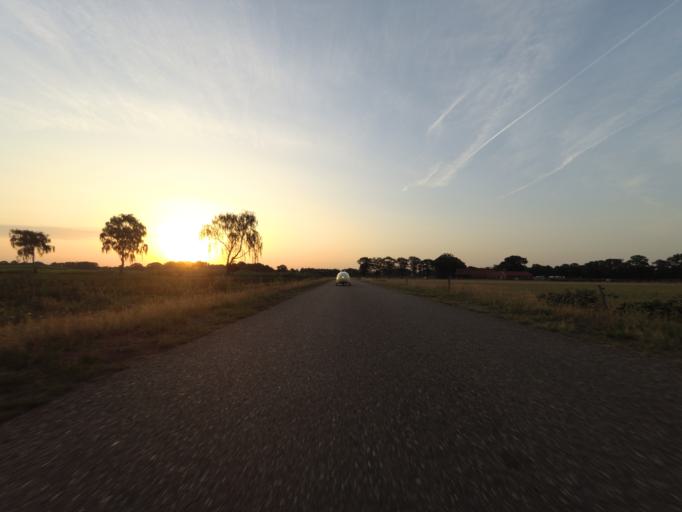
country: NL
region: Overijssel
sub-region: Gemeente Tubbergen
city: Tubbergen
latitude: 52.4104
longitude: 6.7151
